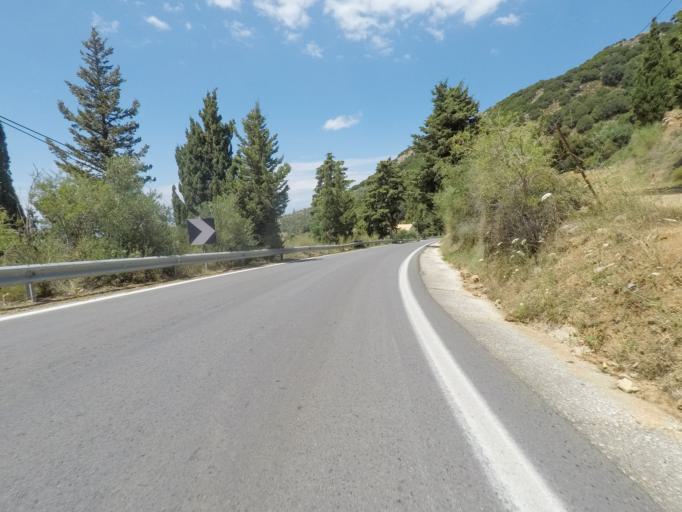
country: GR
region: Crete
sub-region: Nomos Irakleiou
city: Mokhos
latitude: 35.2235
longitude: 25.4620
